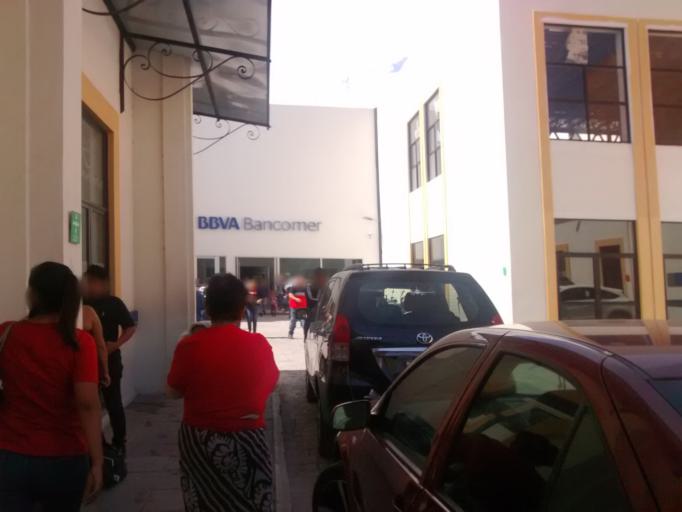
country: MX
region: Puebla
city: Tehuacan
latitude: 18.4615
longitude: -97.3943
